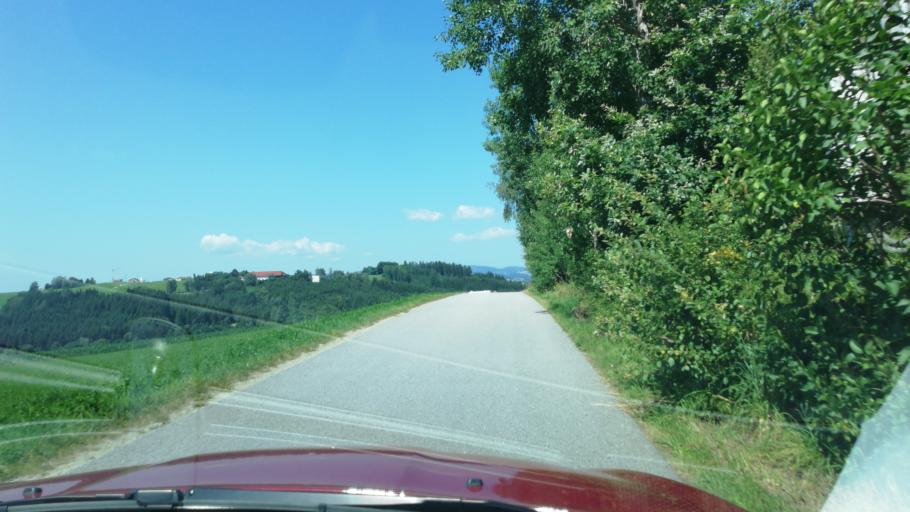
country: AT
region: Upper Austria
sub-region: Politischer Bezirk Rohrbach
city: Kleinzell im Muehlkreis
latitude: 48.4788
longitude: 14.0559
